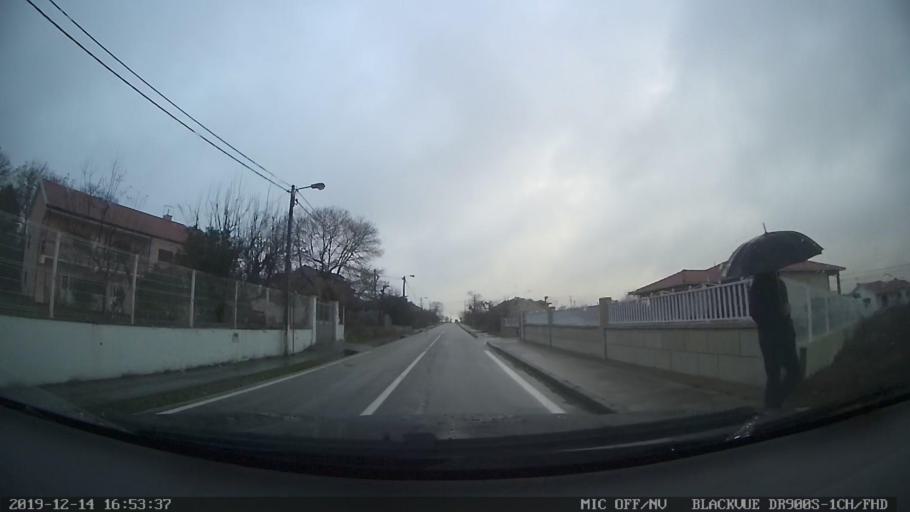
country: PT
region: Vila Real
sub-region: Murca
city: Murca
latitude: 41.4324
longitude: -7.5179
